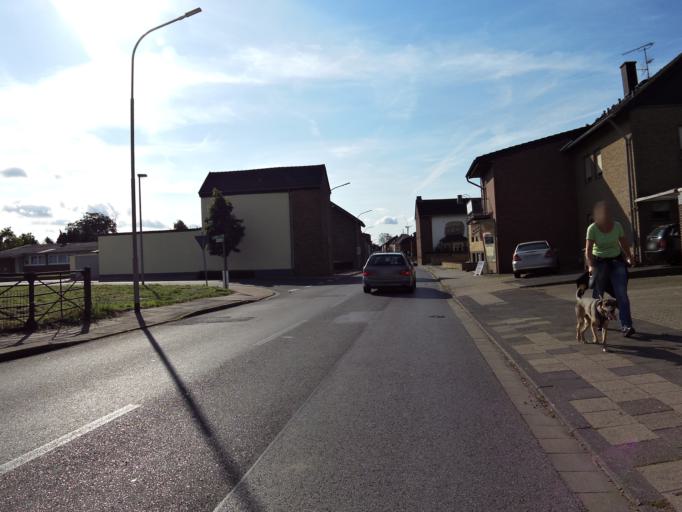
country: DE
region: North Rhine-Westphalia
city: Siersdorf
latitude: 50.8868
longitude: 6.2367
